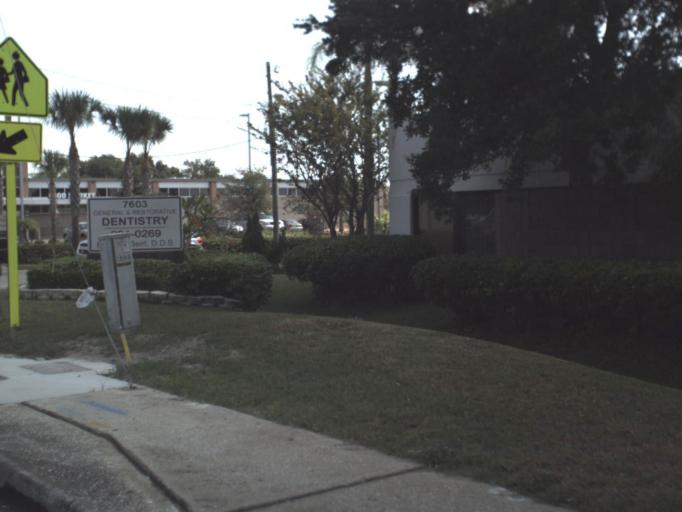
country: US
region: Florida
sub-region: Pinellas County
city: Seminole
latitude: 27.8418
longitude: -82.7870
